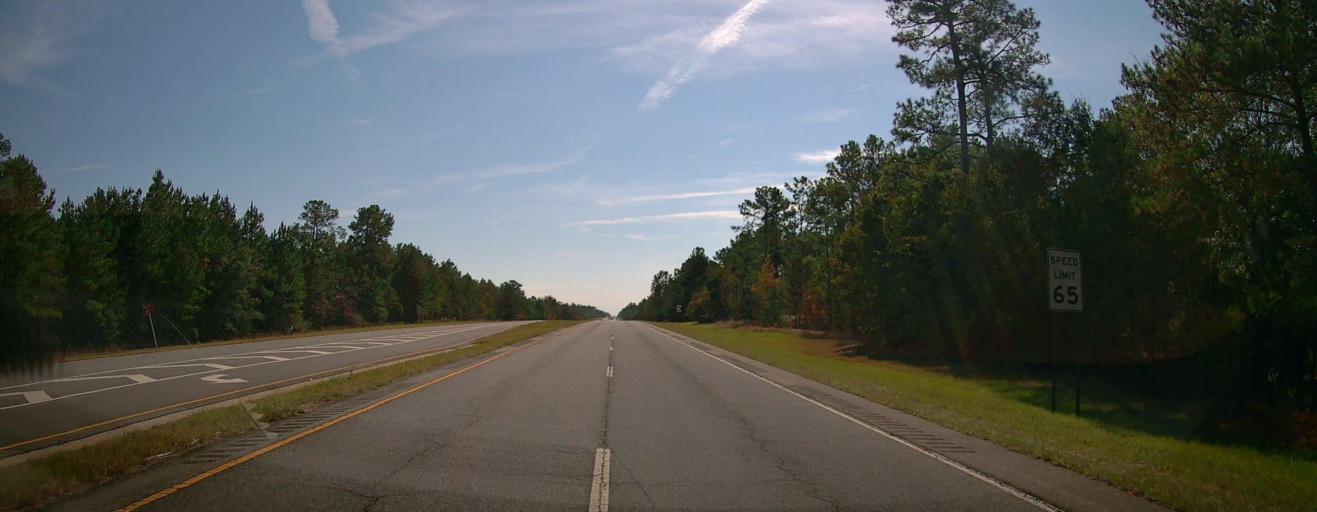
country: US
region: Georgia
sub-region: Lee County
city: Leesburg
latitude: 31.7256
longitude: -83.9874
